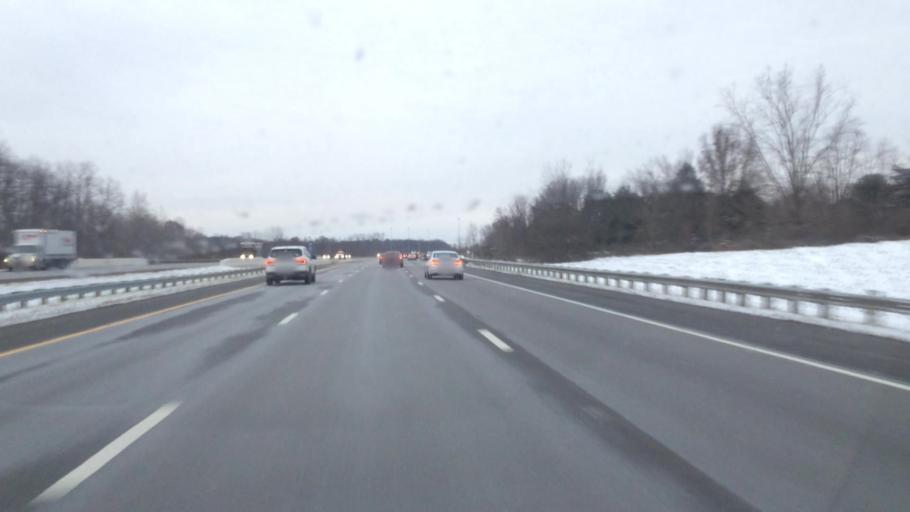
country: US
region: Ohio
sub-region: Medina County
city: Medina
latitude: 41.1699
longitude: -81.7864
